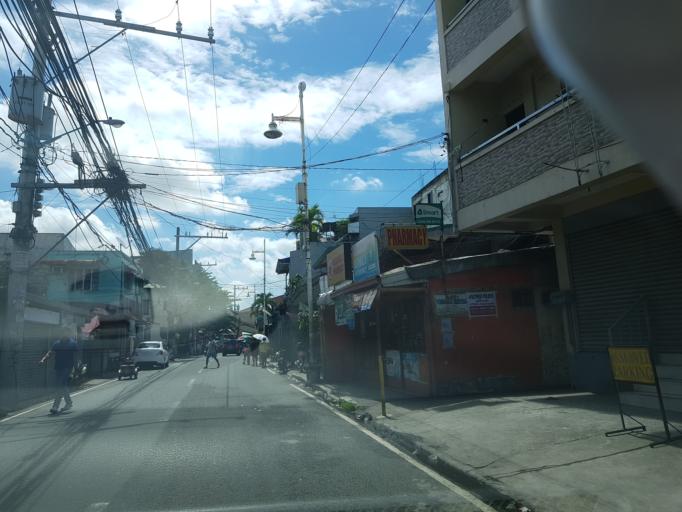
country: PH
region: Calabarzon
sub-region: Province of Rizal
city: Pateros
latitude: 14.5340
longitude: 121.0677
